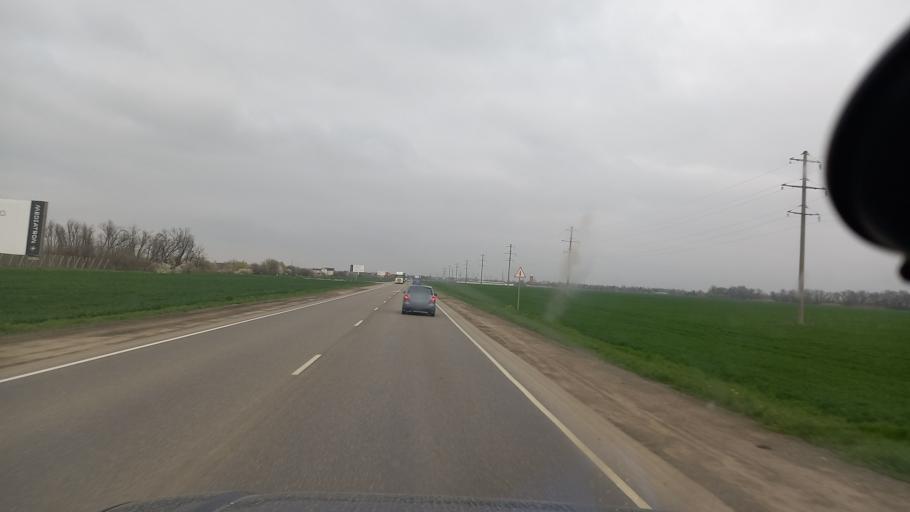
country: RU
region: Krasnodarskiy
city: Slavyansk-na-Kubani
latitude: 45.2458
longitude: 38.0525
